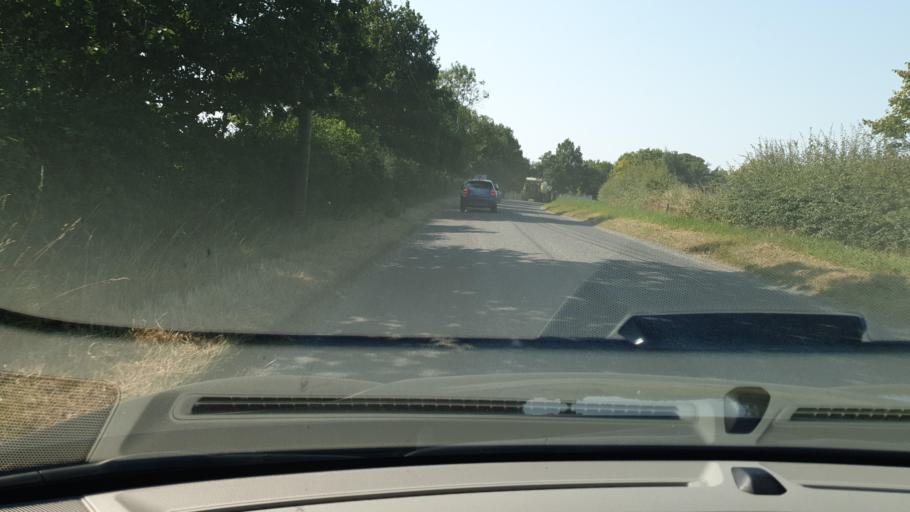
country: IE
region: Leinster
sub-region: An Mhi
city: Trim
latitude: 53.5717
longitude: -6.8258
